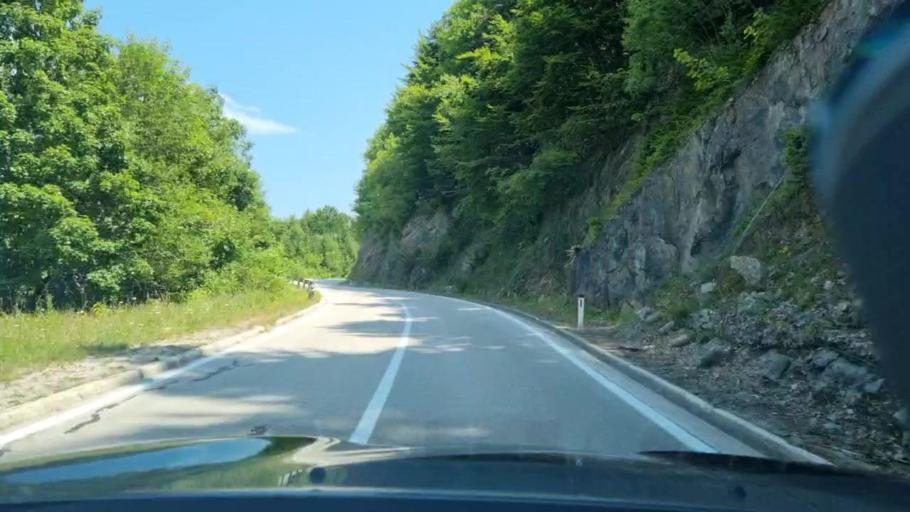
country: BA
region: Federation of Bosnia and Herzegovina
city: Sanica
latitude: 44.5039
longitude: 16.3629
